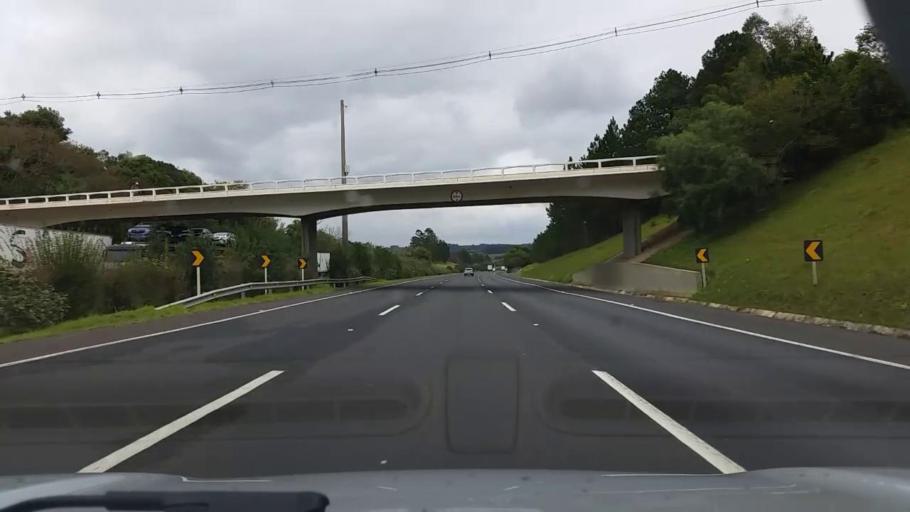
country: BR
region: Rio Grande do Sul
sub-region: Gravatai
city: Gravatai
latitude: -29.9190
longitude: -50.8296
